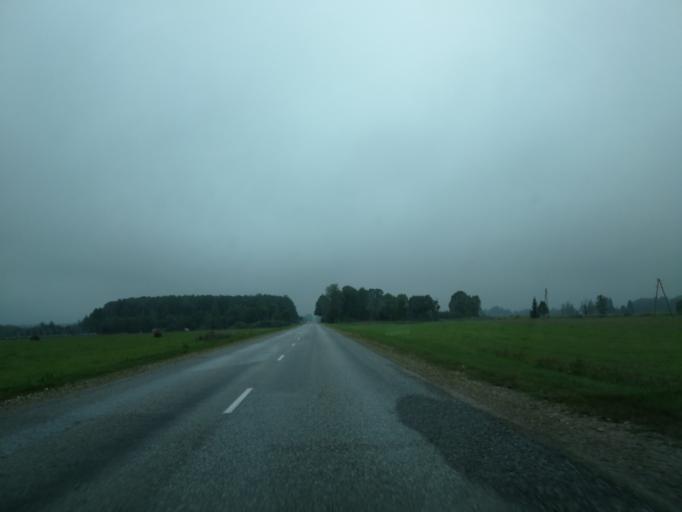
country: LV
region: Varkava
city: Vecvarkava
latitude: 56.3098
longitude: 26.5676
